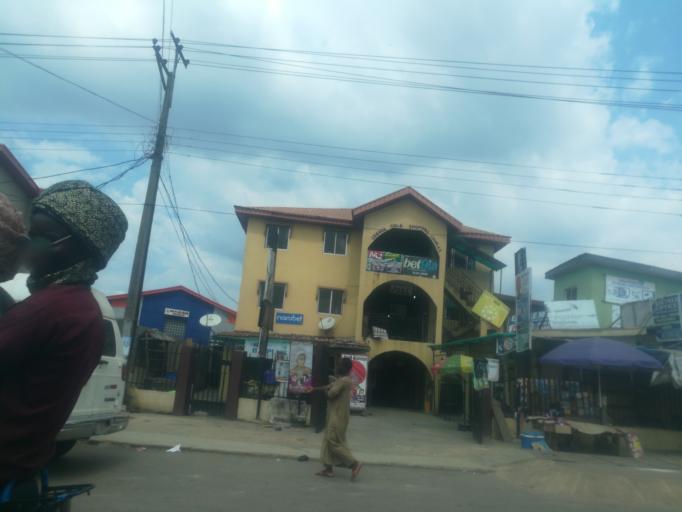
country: NG
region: Oyo
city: Ibadan
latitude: 7.4188
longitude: 3.8602
